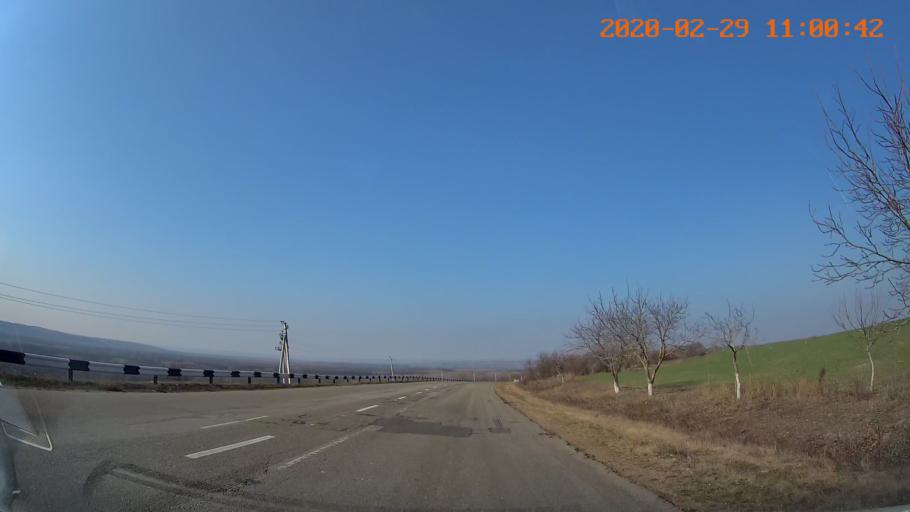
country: MD
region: Telenesti
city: Grigoriopol
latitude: 47.1605
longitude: 29.2729
